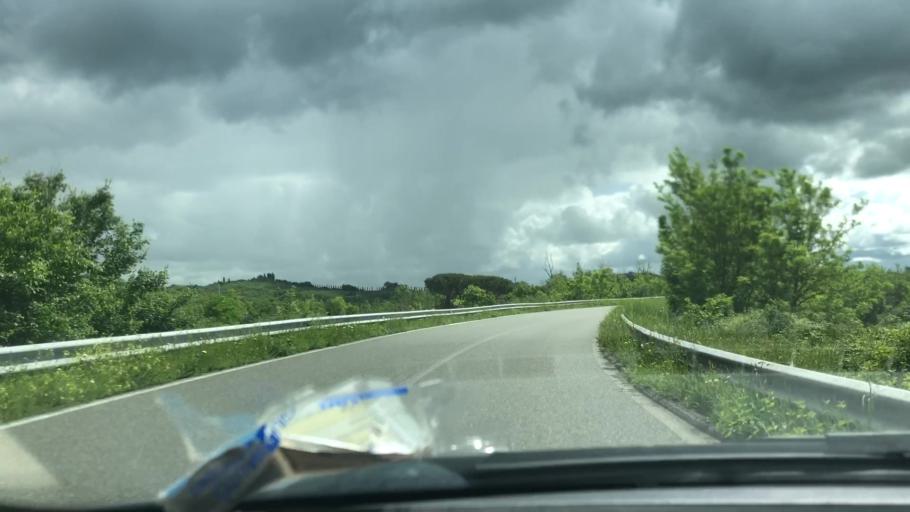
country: IT
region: Tuscany
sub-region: Province of Pisa
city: Saline
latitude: 43.3558
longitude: 10.7824
